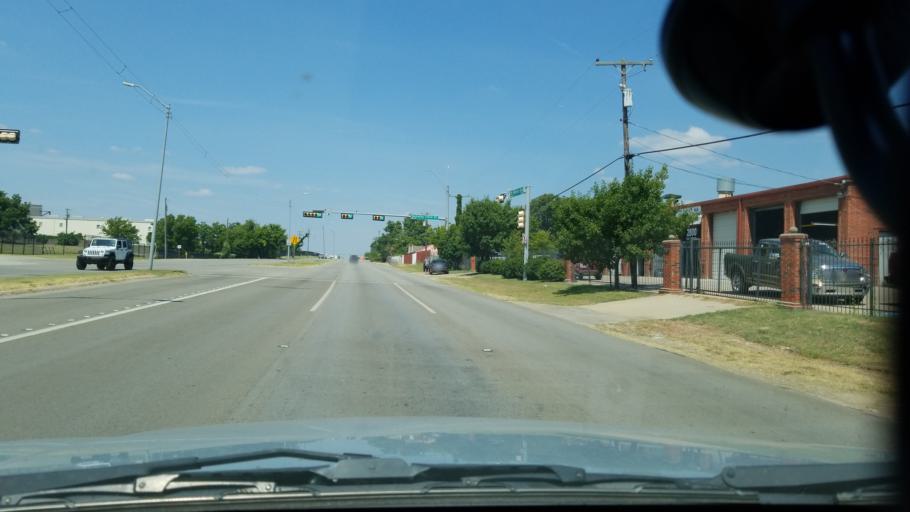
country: US
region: Texas
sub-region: Dallas County
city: Grand Prairie
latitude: 32.7463
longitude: -96.9624
